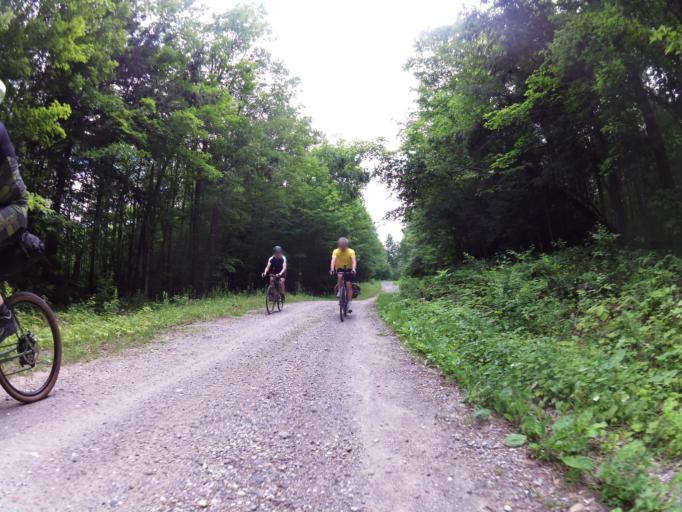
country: CA
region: Ontario
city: Perth
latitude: 45.0265
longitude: -76.5415
